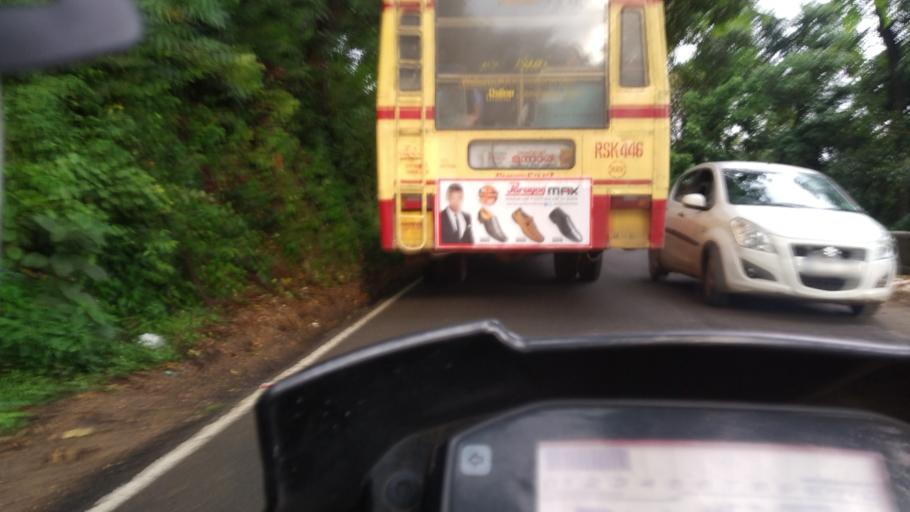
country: IN
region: Kerala
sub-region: Idukki
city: Kuttampuzha
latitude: 10.0660
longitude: 76.7738
